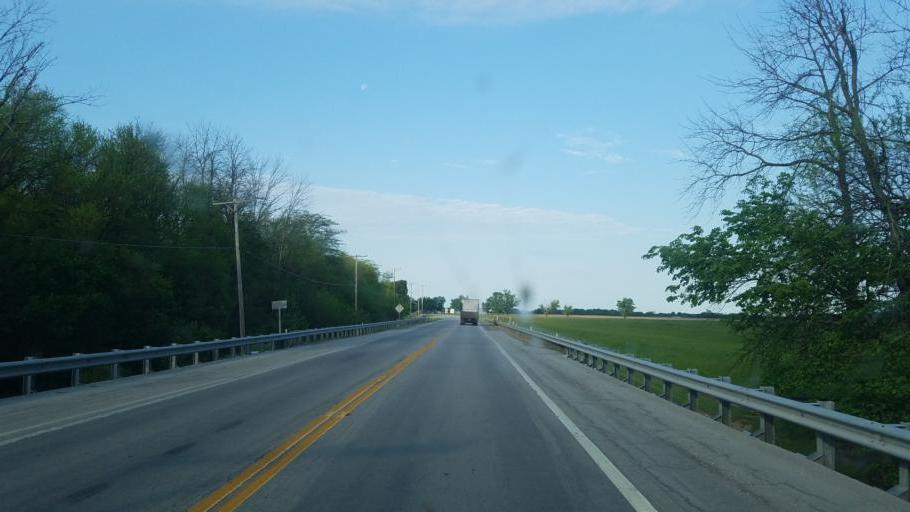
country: US
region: Ohio
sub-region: Fayette County
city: Washington Court House
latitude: 39.5630
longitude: -83.4088
